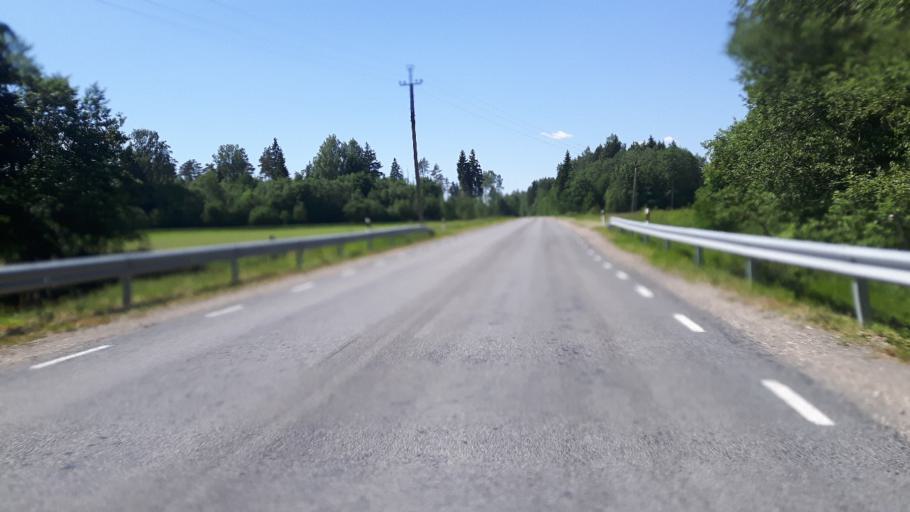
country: EE
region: Paernumaa
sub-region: Tootsi vald
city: Tootsi
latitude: 58.4982
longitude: 24.8628
